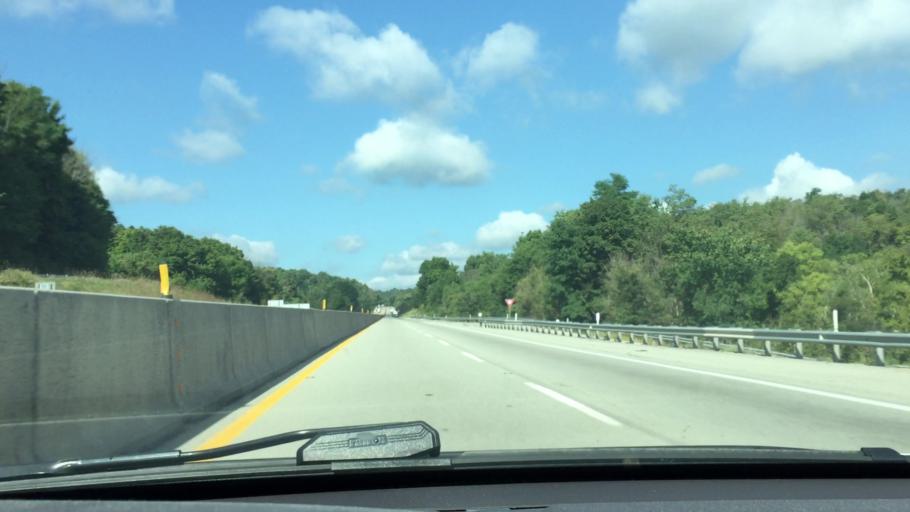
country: US
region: Pennsylvania
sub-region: Washington County
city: Ellsworth
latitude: 40.1659
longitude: -80.0854
